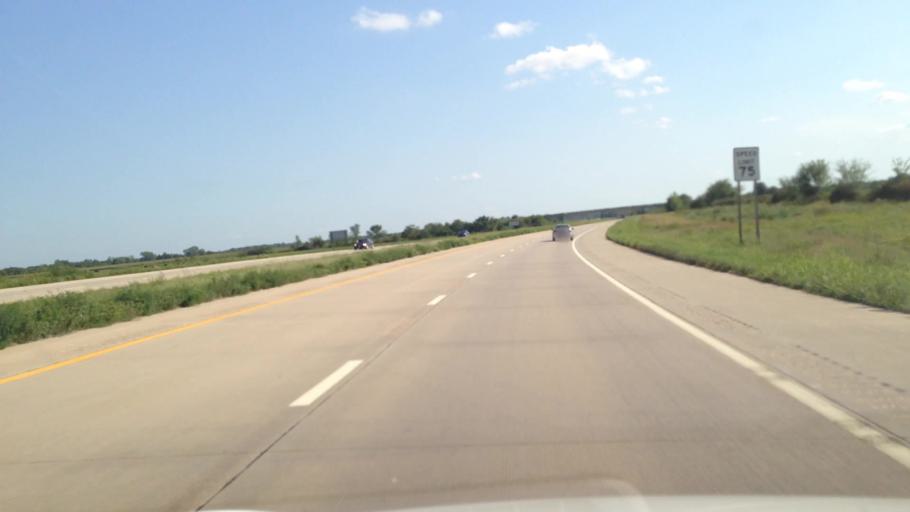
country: US
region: Kansas
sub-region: Bourbon County
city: Fort Scott
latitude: 37.9271
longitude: -94.7047
